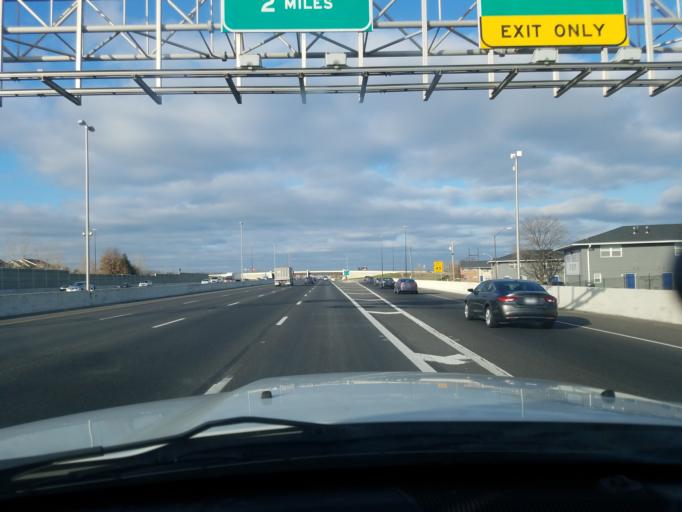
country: US
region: Indiana
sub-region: Marion County
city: Speedway
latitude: 39.8187
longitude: -86.2754
